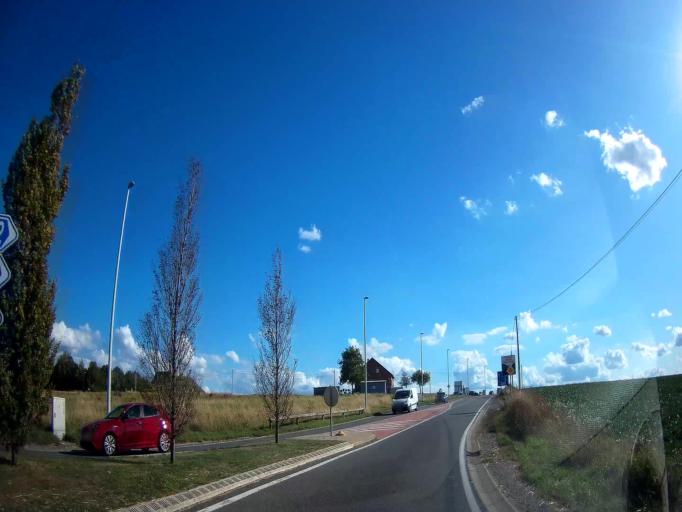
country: BE
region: Wallonia
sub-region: Province de Namur
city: Mettet
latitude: 50.3206
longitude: 4.7398
